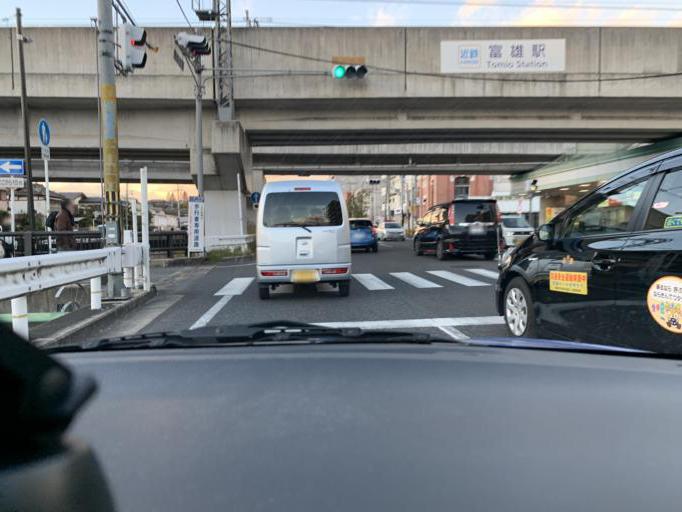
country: JP
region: Nara
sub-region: Ikoma-shi
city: Ikoma
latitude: 34.6938
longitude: 135.7340
